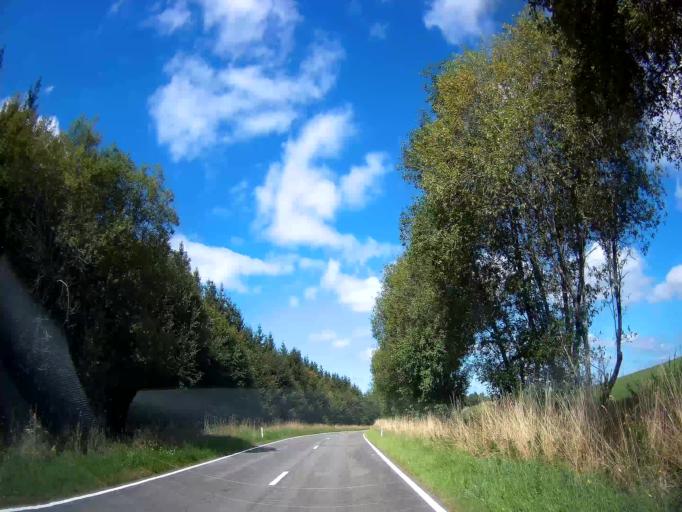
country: BE
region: Wallonia
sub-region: Province du Luxembourg
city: Bastogne
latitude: 50.0369
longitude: 5.6936
